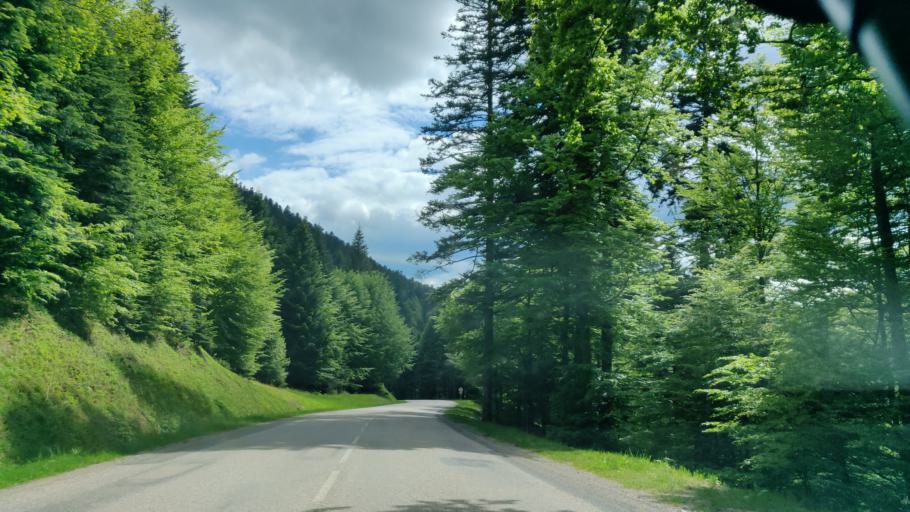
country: FR
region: Lorraine
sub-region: Departement des Vosges
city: Xonrupt-Longemer
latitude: 48.0273
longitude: 6.9607
